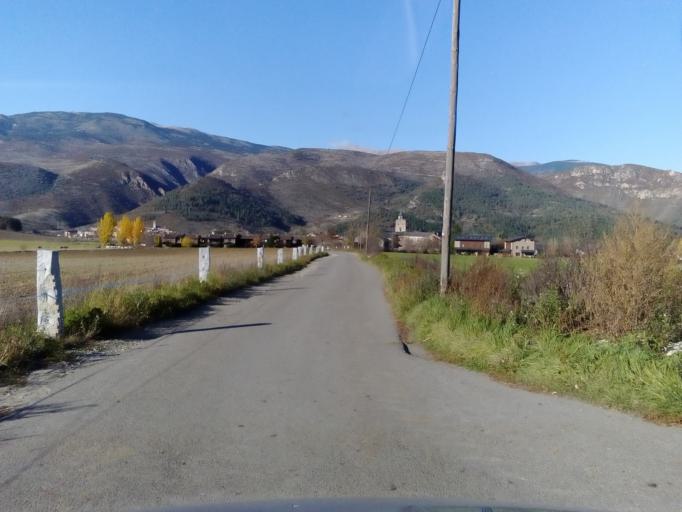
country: ES
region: Catalonia
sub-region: Provincia de Lleida
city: Bellver de Cerdanya
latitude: 42.3595
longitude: 1.7810
